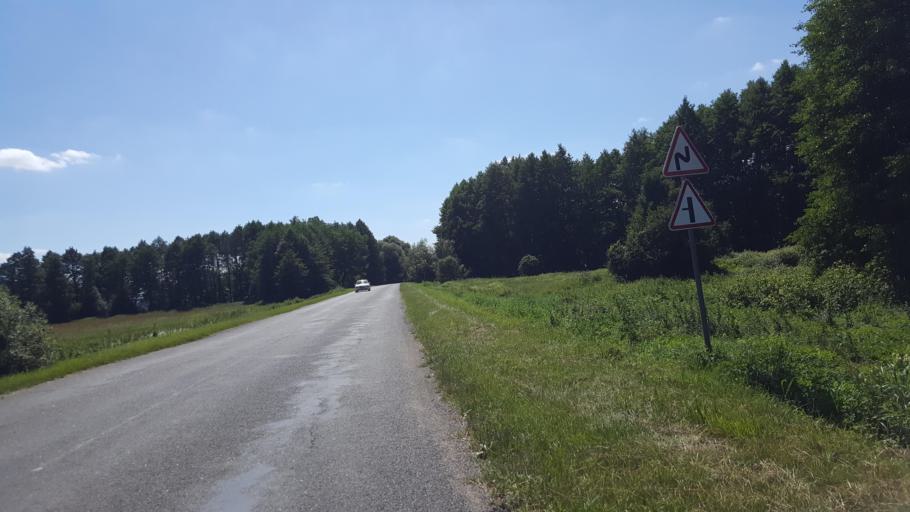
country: BY
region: Brest
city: Charnawchytsy
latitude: 52.3229
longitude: 23.6142
